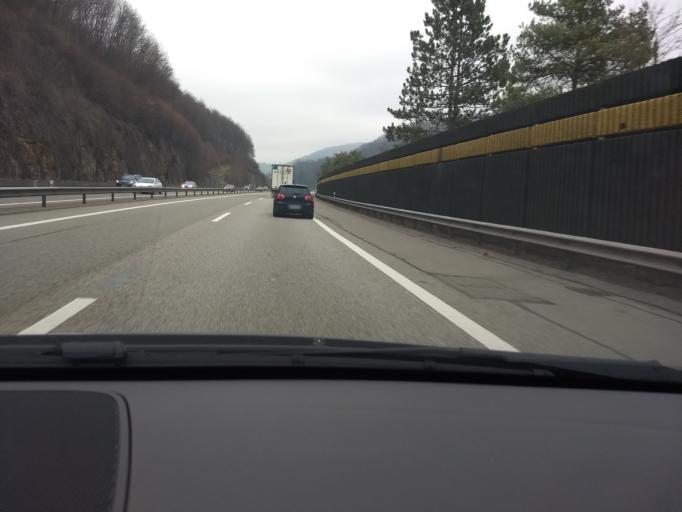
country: CH
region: Basel-Landschaft
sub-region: Bezirk Waldenburg
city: Diegten
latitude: 47.4183
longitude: 7.8085
